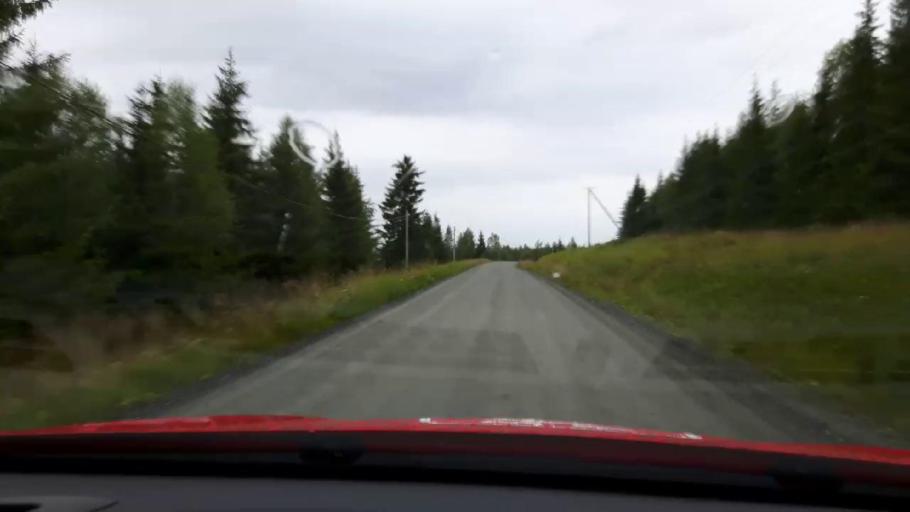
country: SE
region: Jaemtland
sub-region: Are Kommun
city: Are
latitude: 63.4111
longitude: 12.8300
